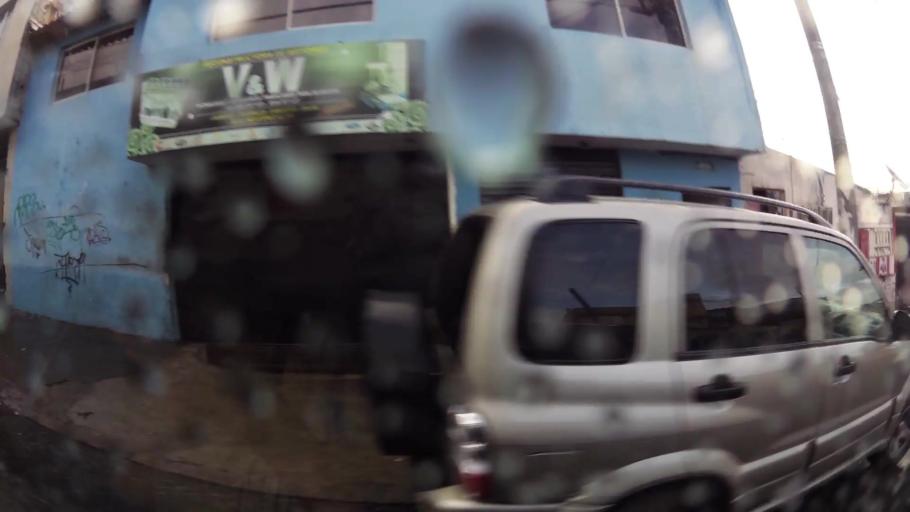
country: EC
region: Pichincha
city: Quito
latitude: -0.1056
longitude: -78.4948
